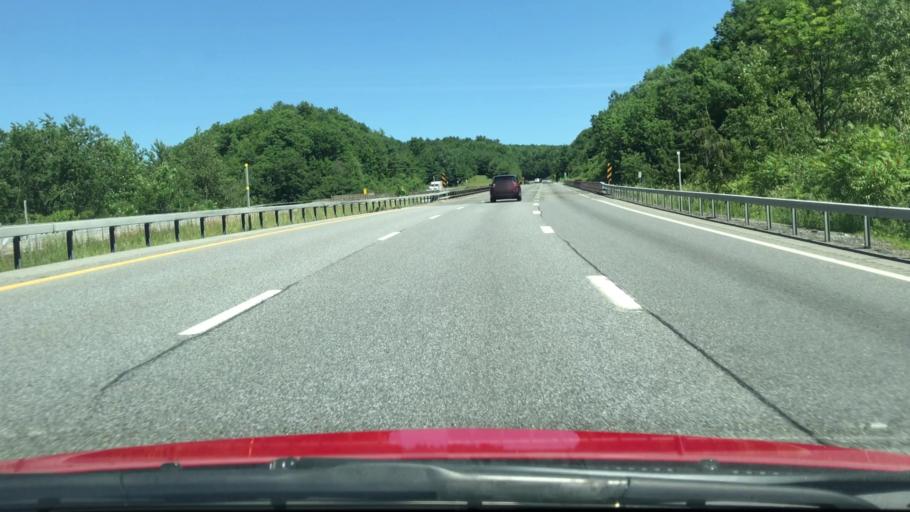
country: US
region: New York
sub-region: Warren County
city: Warrensburg
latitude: 43.4519
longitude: -73.7348
